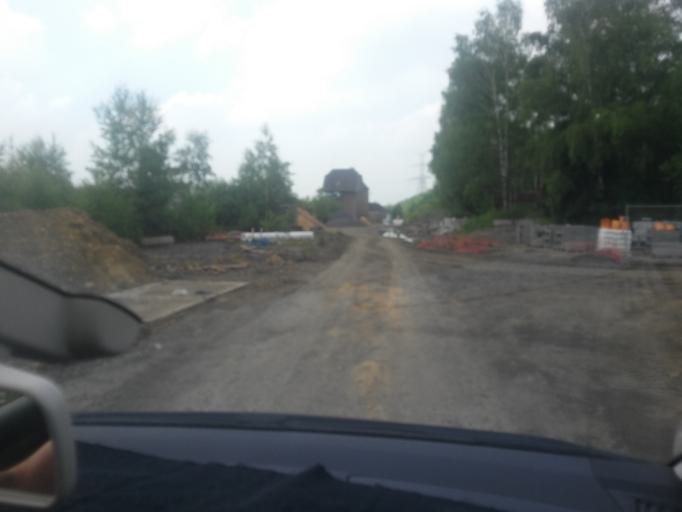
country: BE
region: Wallonia
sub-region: Province du Luxembourg
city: Arlon
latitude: 49.6914
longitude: 5.7552
